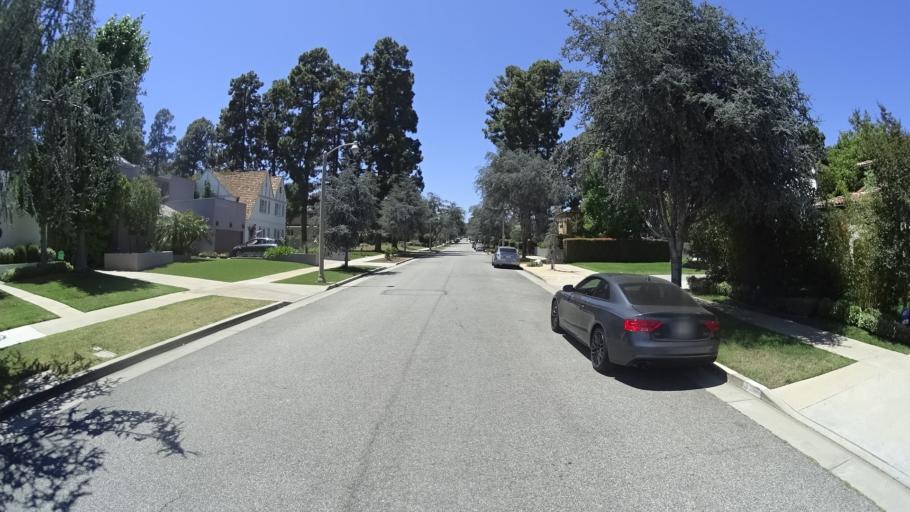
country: US
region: California
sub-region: Los Angeles County
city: Santa Monica
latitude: 34.0415
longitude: -118.4855
